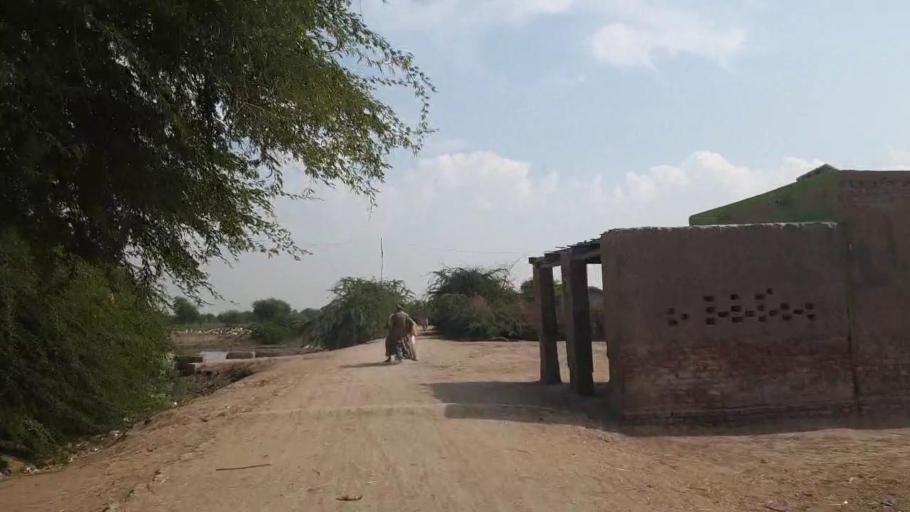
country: PK
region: Sindh
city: Tando Bago
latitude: 24.9355
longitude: 69.0005
